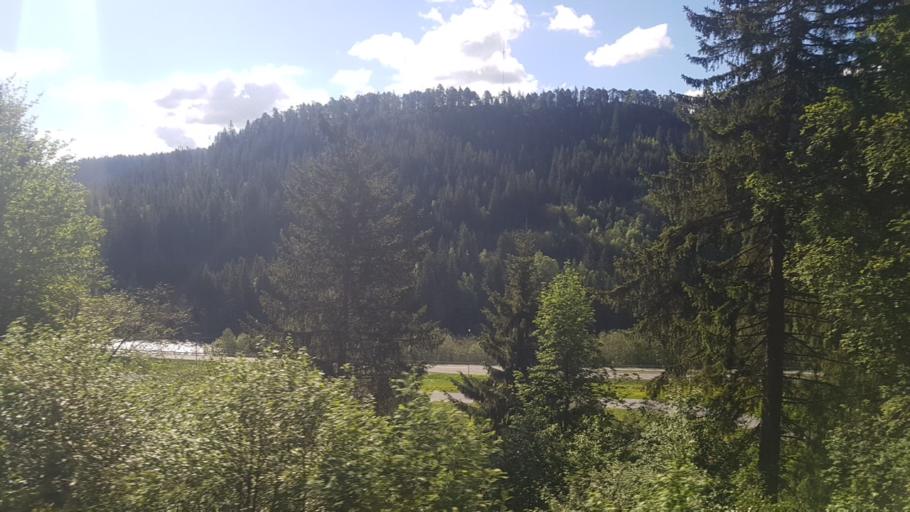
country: NO
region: Sor-Trondelag
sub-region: Midtre Gauldal
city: Storen
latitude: 63.0236
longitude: 10.2577
